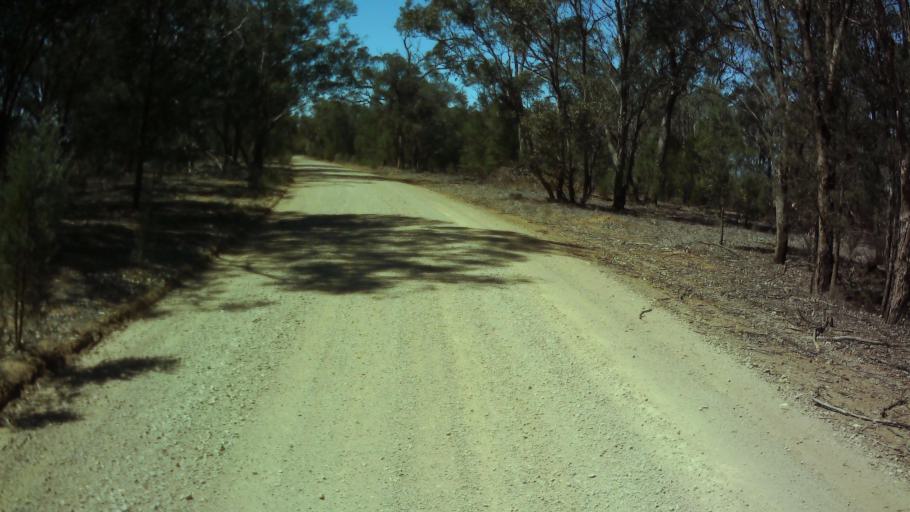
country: AU
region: New South Wales
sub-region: Weddin
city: Grenfell
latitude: -33.8585
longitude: 148.0868
